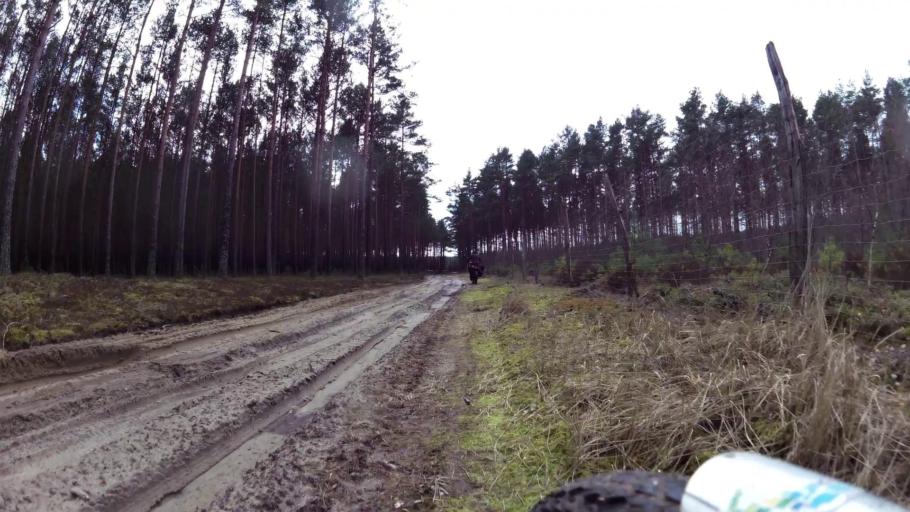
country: PL
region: Pomeranian Voivodeship
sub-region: Powiat bytowski
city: Kolczyglowy
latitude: 54.1660
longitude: 17.1946
